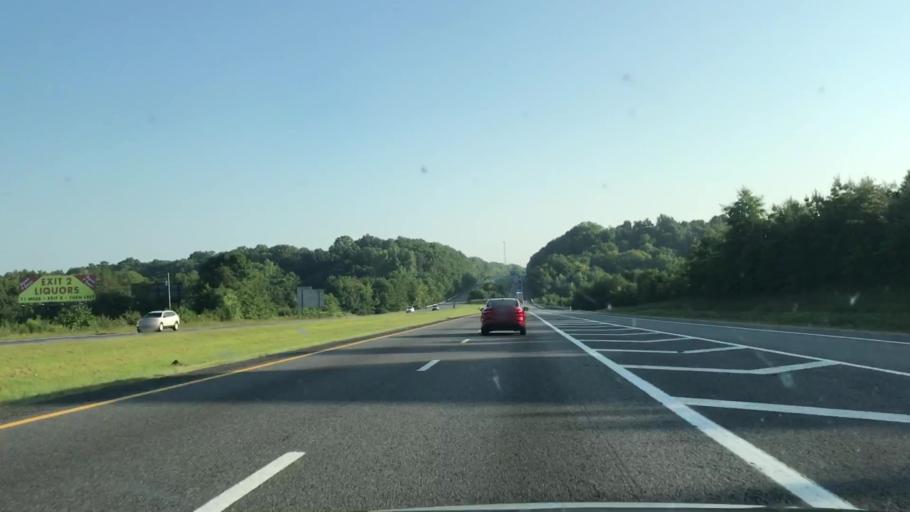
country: US
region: Tennessee
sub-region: Robertson County
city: Cross Plains
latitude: 36.5310
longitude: -86.6415
